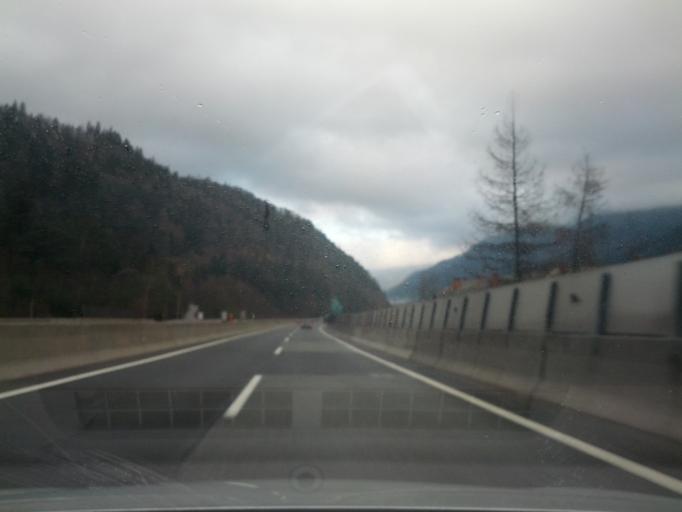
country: SI
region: Jesenice
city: Jesenice
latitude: 46.4335
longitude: 14.0467
